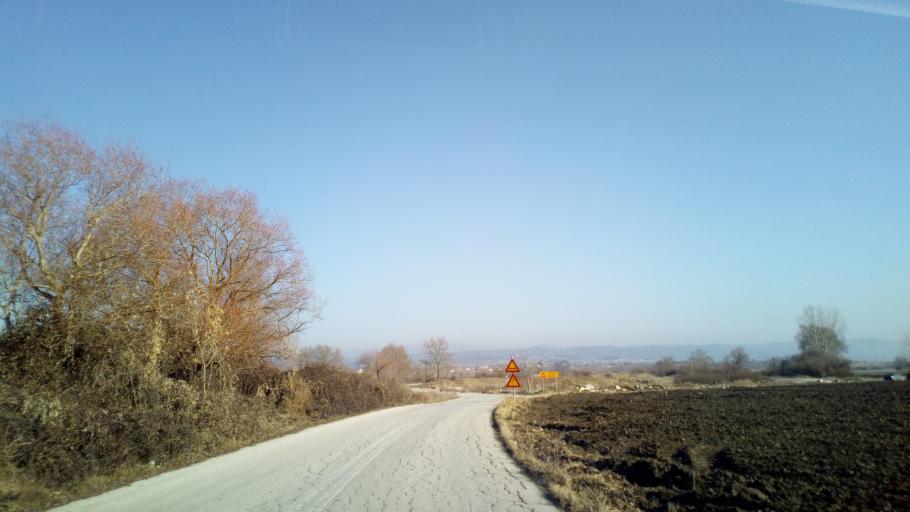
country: GR
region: Central Macedonia
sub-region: Nomos Thessalonikis
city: Gerakarou
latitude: 40.6570
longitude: 23.2506
